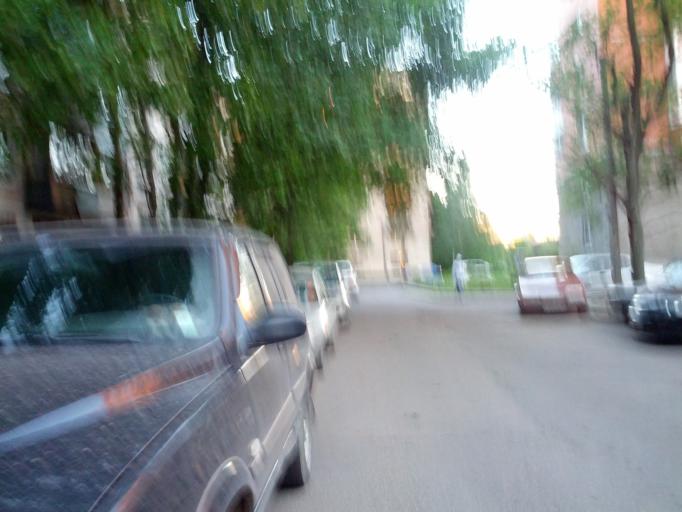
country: RU
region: St.-Petersburg
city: Obukhovo
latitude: 59.9062
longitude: 30.4695
